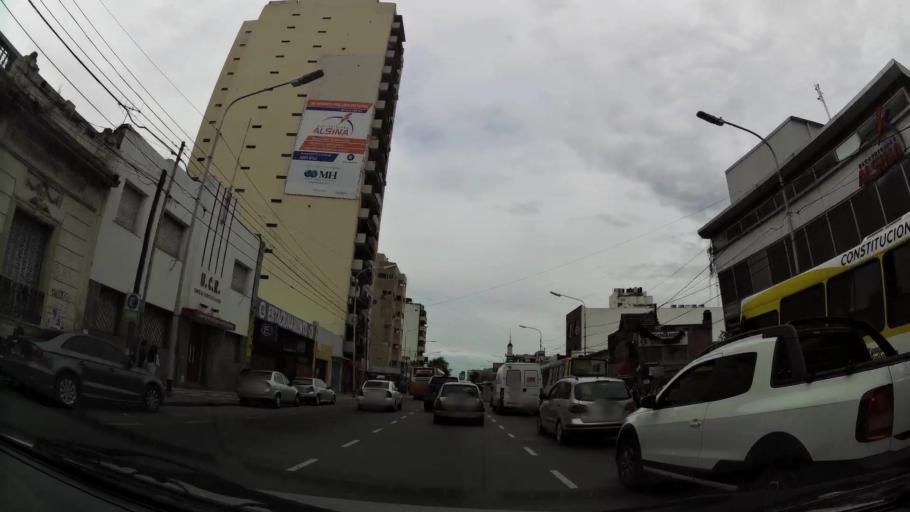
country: AR
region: Buenos Aires
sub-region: Partido de Avellaneda
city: Avellaneda
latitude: -34.6646
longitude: -58.3662
